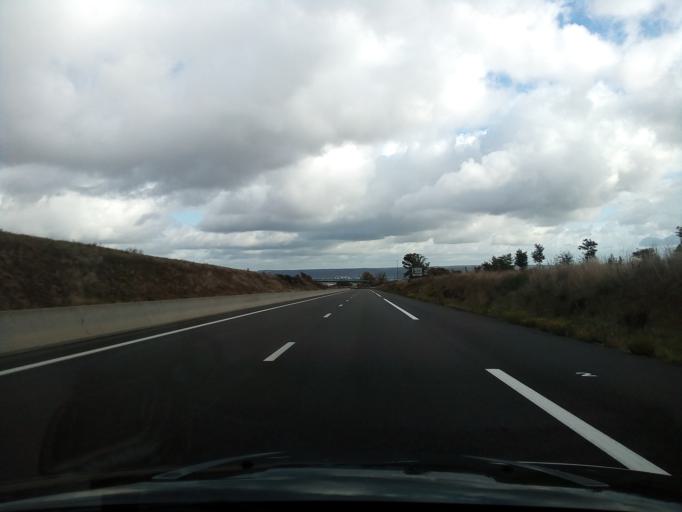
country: FR
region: Auvergne
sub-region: Departement de l'Allier
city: Quinssaines
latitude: 46.3207
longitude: 2.5175
